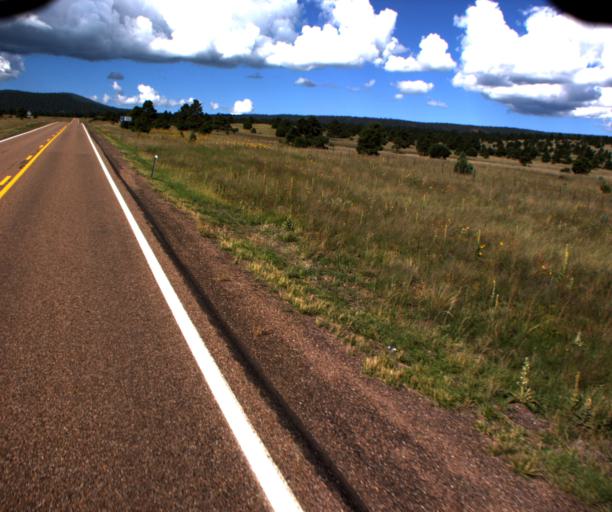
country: US
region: Arizona
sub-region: Apache County
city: Eagar
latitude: 34.0853
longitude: -109.4443
